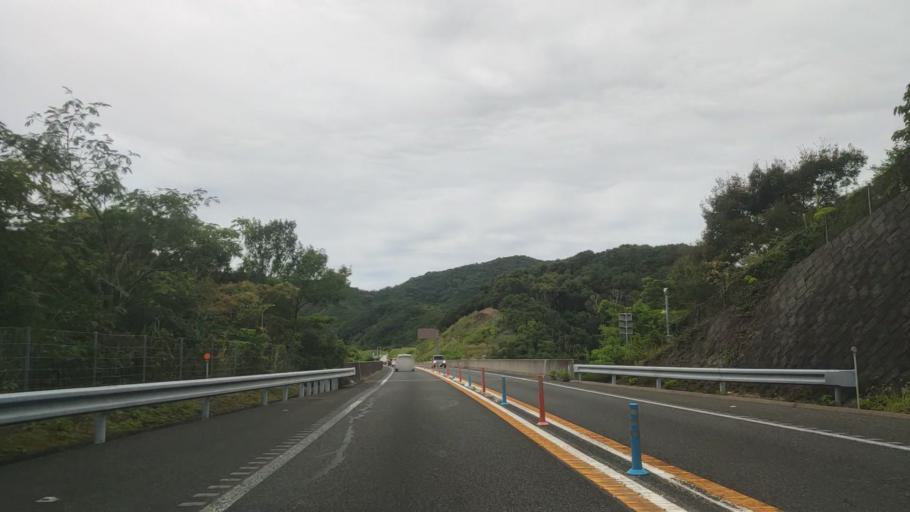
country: JP
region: Wakayama
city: Tanabe
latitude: 33.8012
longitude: 135.2751
